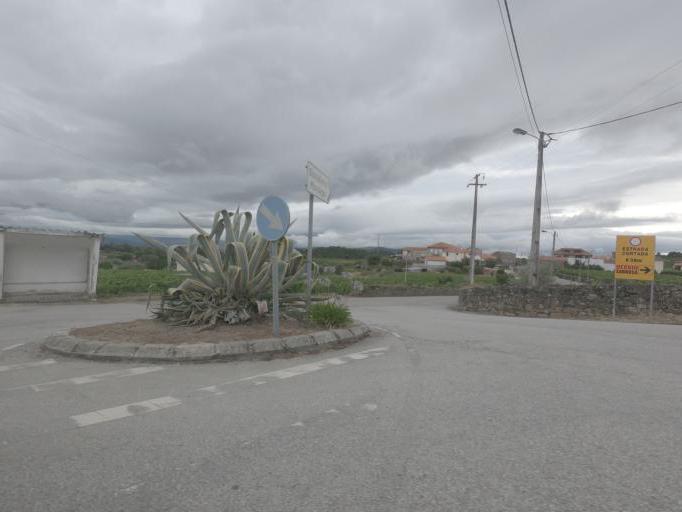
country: PT
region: Vila Real
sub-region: Sabrosa
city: Sabrosa
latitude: 41.2751
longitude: -7.5081
